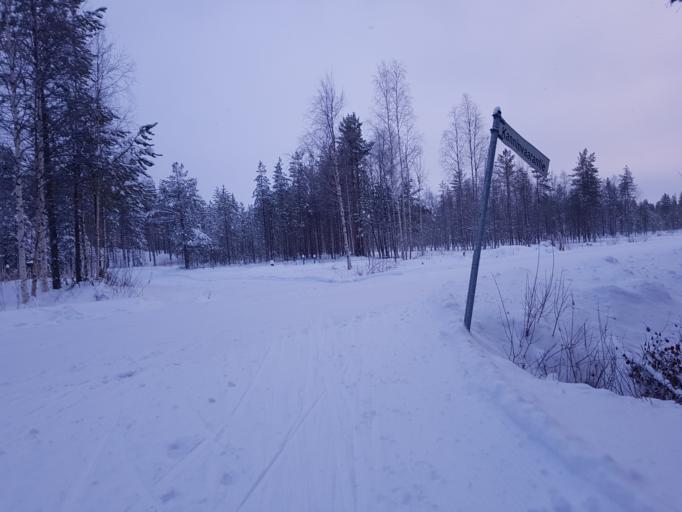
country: FI
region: Kainuu
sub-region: Kehys-Kainuu
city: Kuhmo
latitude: 64.1173
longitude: 29.5735
